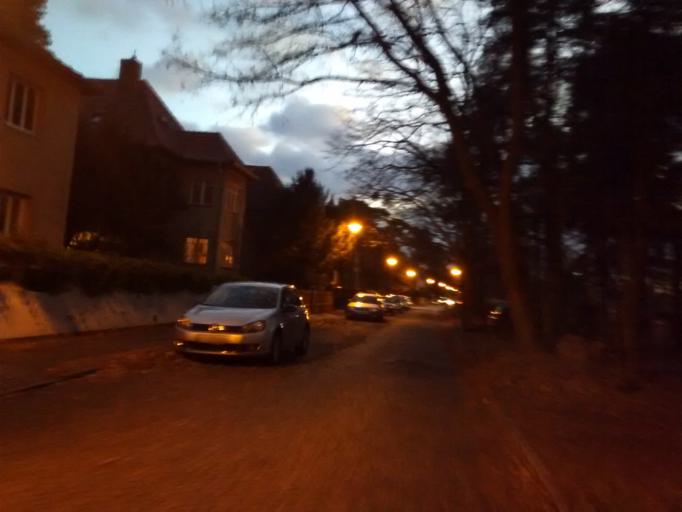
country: DE
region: Brandenburg
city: Potsdam
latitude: 52.3902
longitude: 13.1145
